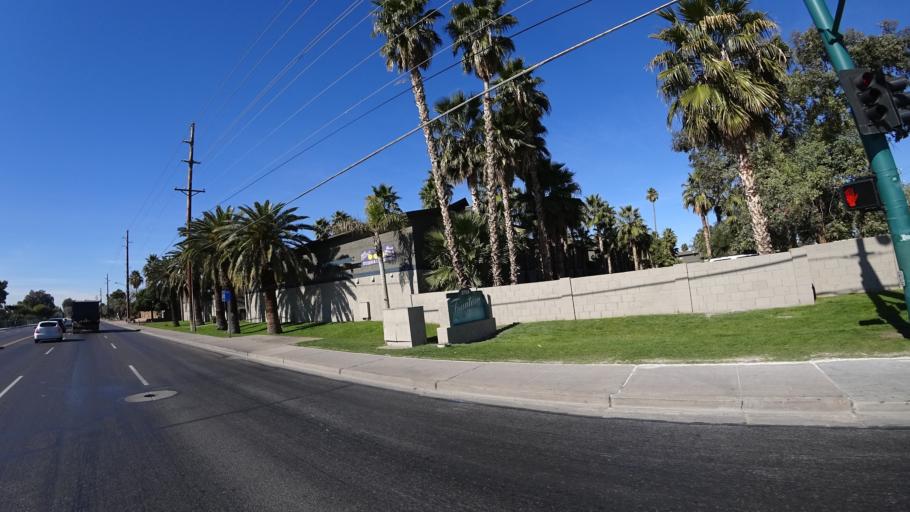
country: US
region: Arizona
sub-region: Maricopa County
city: Glendale
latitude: 33.5095
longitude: -112.1386
